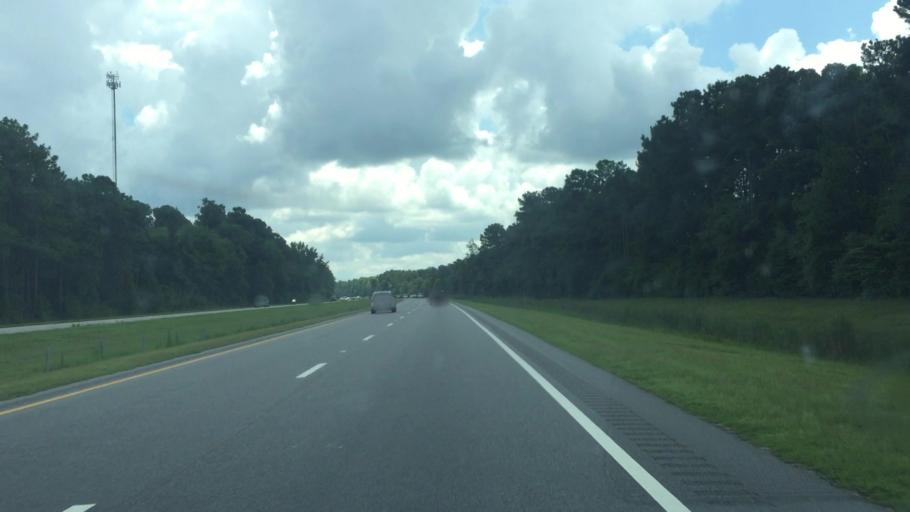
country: US
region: North Carolina
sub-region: Columbus County
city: Chadbourn
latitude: 34.4143
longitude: -78.9345
